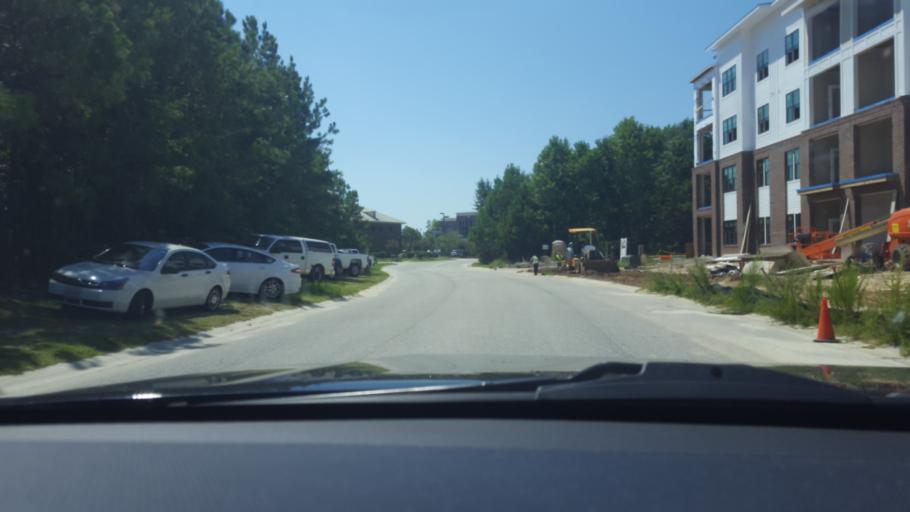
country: US
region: North Carolina
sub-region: New Hanover County
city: Ogden
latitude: 34.2424
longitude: -77.8237
